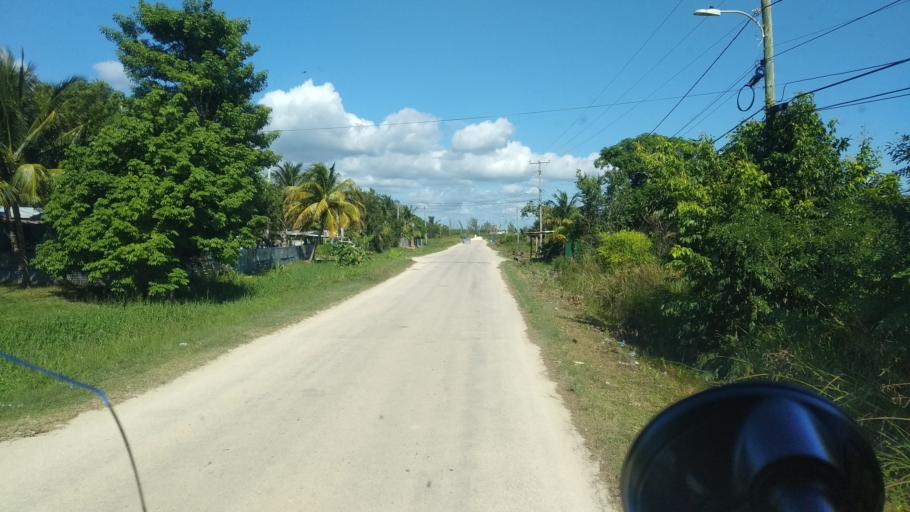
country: BZ
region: Belize
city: Belize City
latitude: 17.5585
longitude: -88.3030
